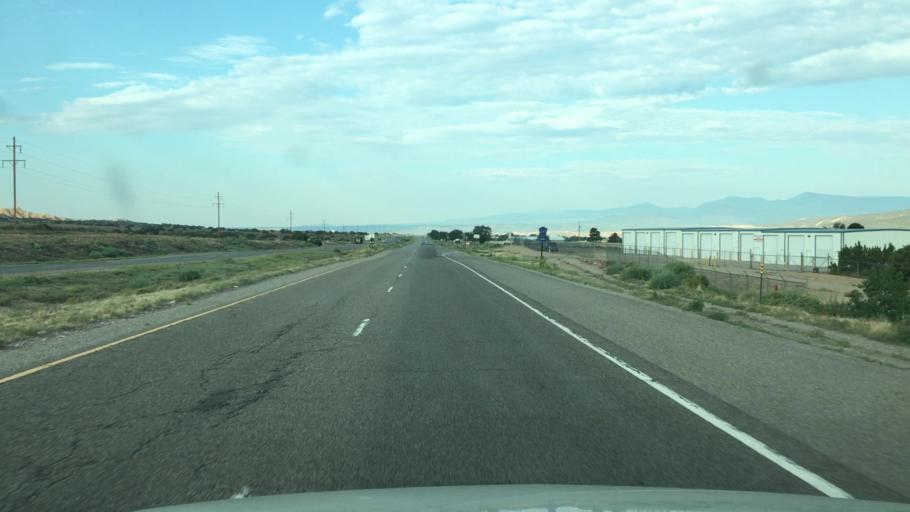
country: US
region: New Mexico
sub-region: Rio Arriba County
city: Ohkay Owingeh
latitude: 36.1351
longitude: -105.9968
